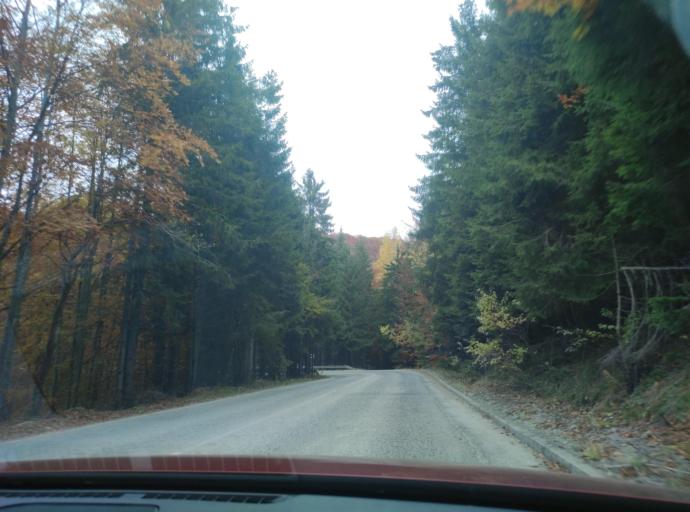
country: BG
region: Sofiya
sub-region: Obshtina Godech
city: Godech
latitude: 43.1131
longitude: 23.1125
